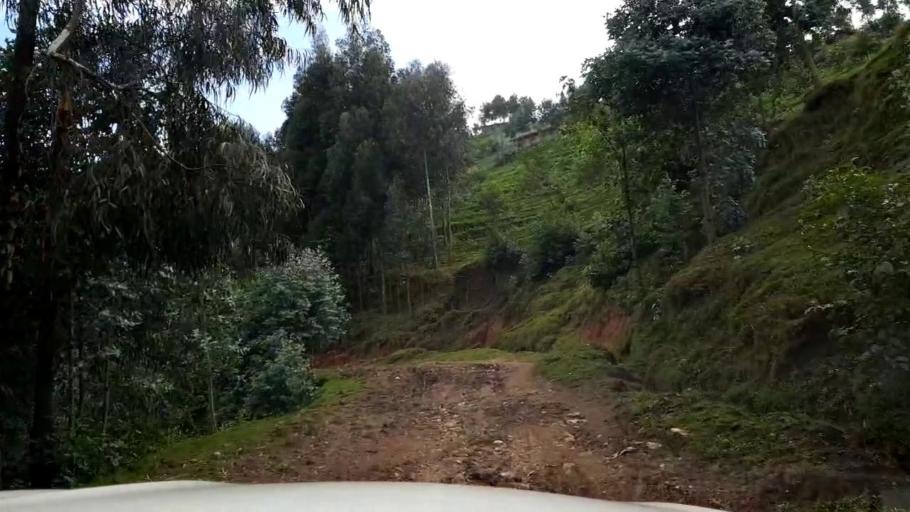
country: RW
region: Western Province
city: Gisenyi
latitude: -1.7195
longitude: 29.3903
